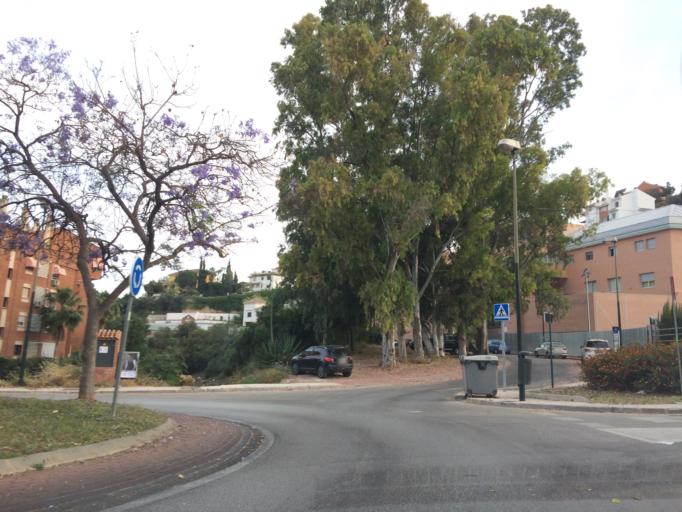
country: ES
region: Andalusia
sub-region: Provincia de Malaga
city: Malaga
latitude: 36.7324
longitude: -4.3977
